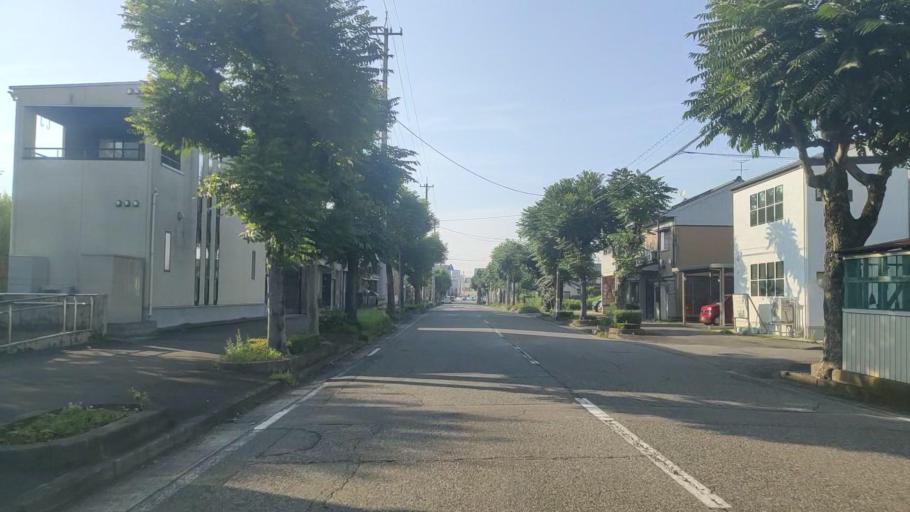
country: JP
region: Fukui
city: Fukui-shi
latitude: 36.0537
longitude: 136.2311
